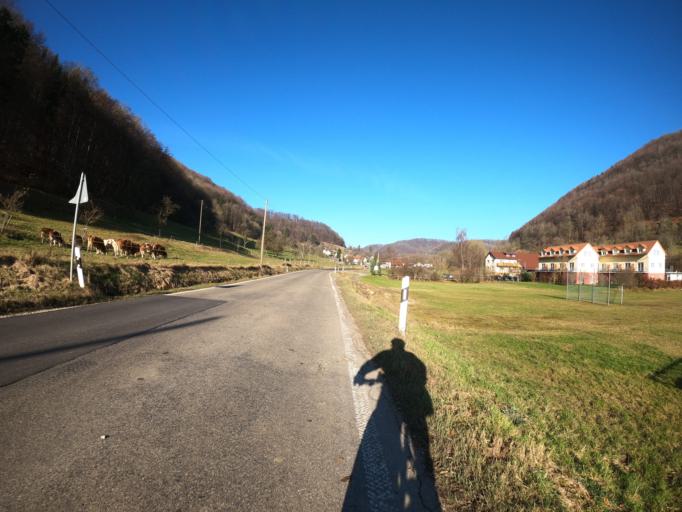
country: DE
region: Baden-Wuerttemberg
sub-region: Regierungsbezirk Stuttgart
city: Bad Ditzenbach
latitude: 48.6091
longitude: 9.6788
